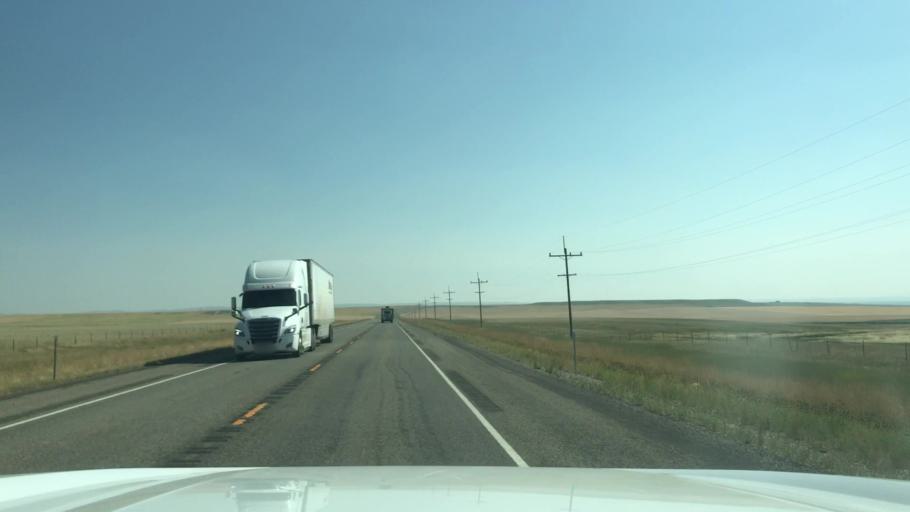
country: US
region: Montana
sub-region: Wheatland County
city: Harlowton
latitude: 46.4980
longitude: -109.7661
